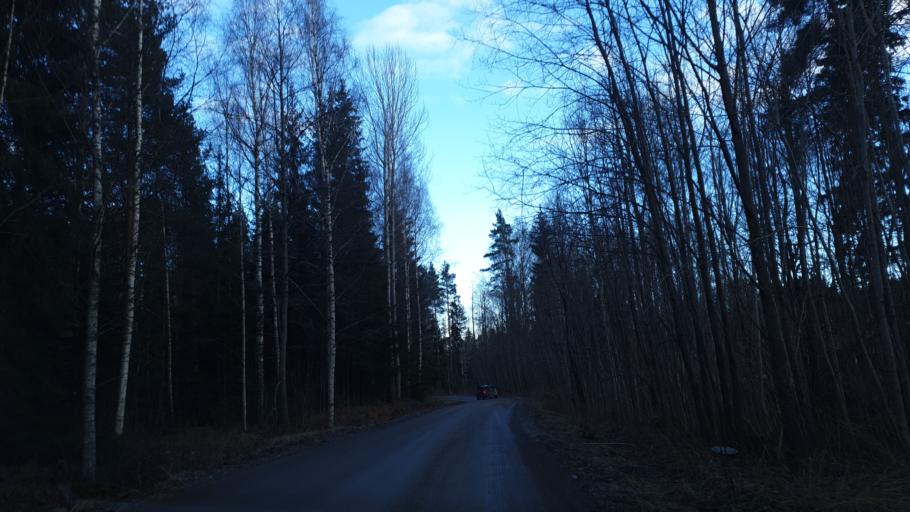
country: SE
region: OErebro
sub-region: Orebro Kommun
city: Garphyttan
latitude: 59.3510
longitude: 14.9882
